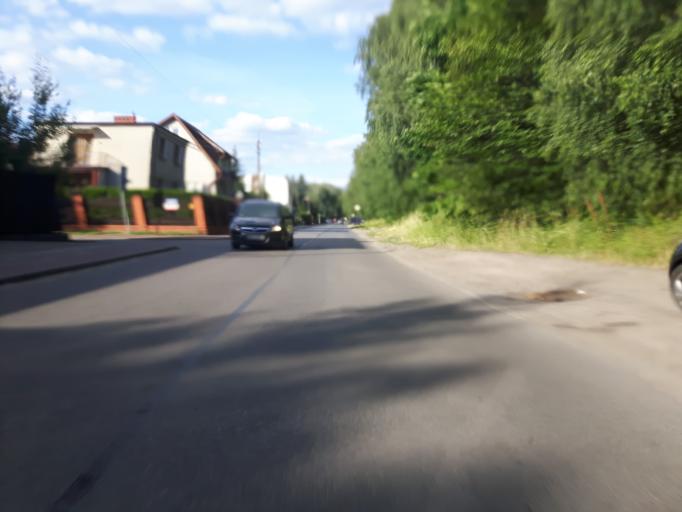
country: PL
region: Masovian Voivodeship
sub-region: Powiat wolominski
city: Zabki
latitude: 52.2947
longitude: 21.1175
